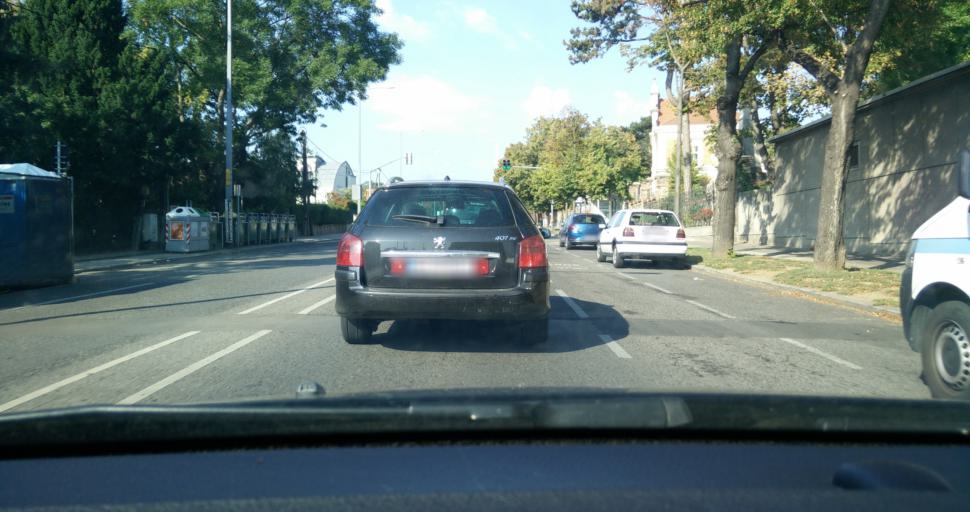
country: AT
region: Vienna
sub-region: Wien Stadt
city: Vienna
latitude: 48.2084
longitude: 16.3011
